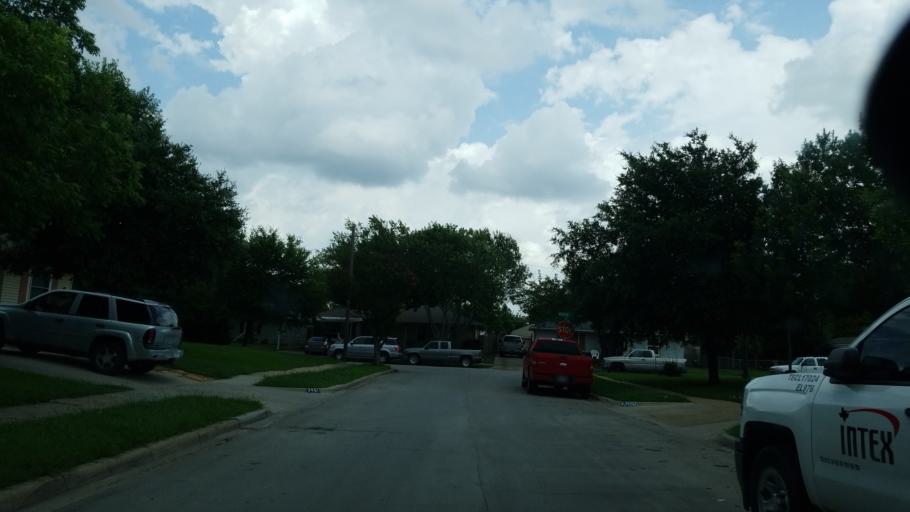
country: US
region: Texas
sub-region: Dallas County
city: Farmers Branch
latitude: 32.8742
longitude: -96.8623
